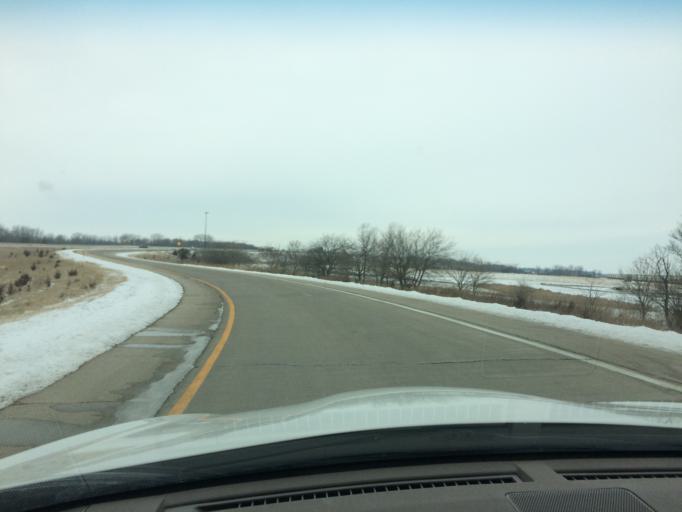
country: US
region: Illinois
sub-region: LaSalle County
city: Mendota
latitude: 41.4709
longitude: -89.0477
